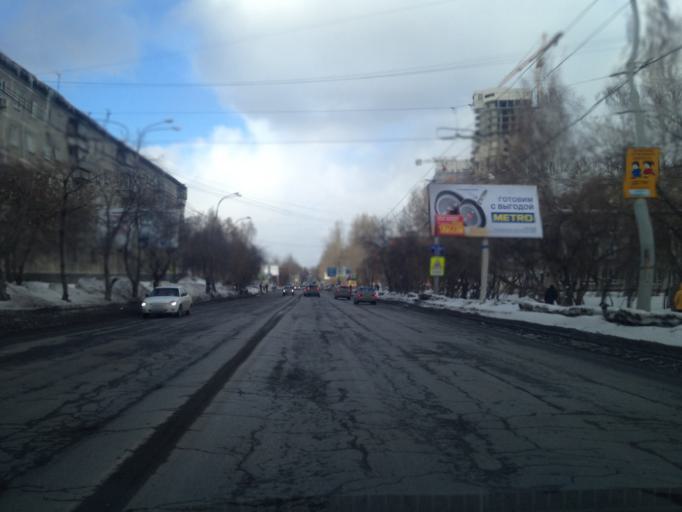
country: RU
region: Sverdlovsk
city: Yekaterinburg
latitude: 56.8595
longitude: 60.6535
